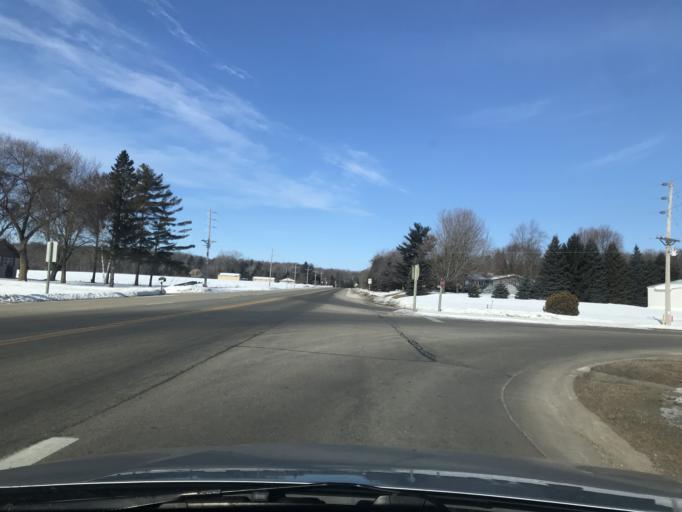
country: US
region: Wisconsin
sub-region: Oconto County
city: Oconto Falls
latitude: 44.8850
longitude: -88.1560
